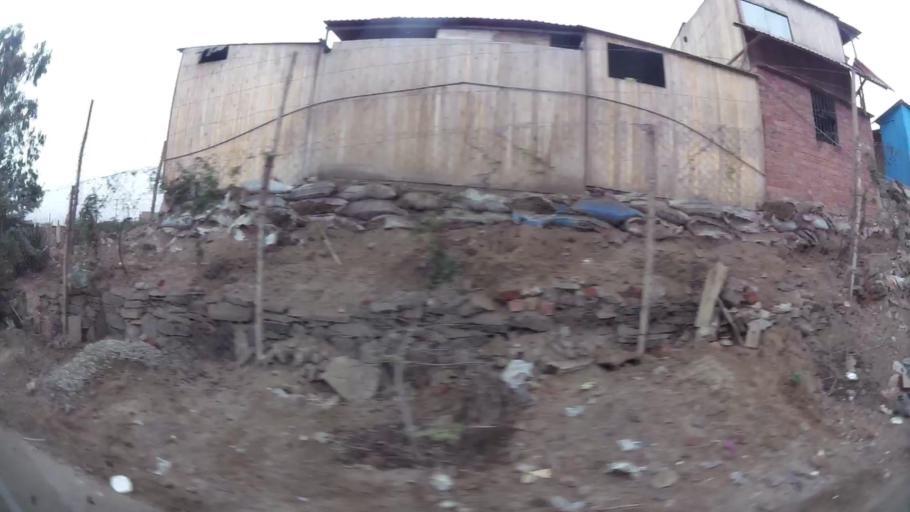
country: PE
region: Lima
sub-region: Lima
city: Surco
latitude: -12.1824
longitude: -76.9578
